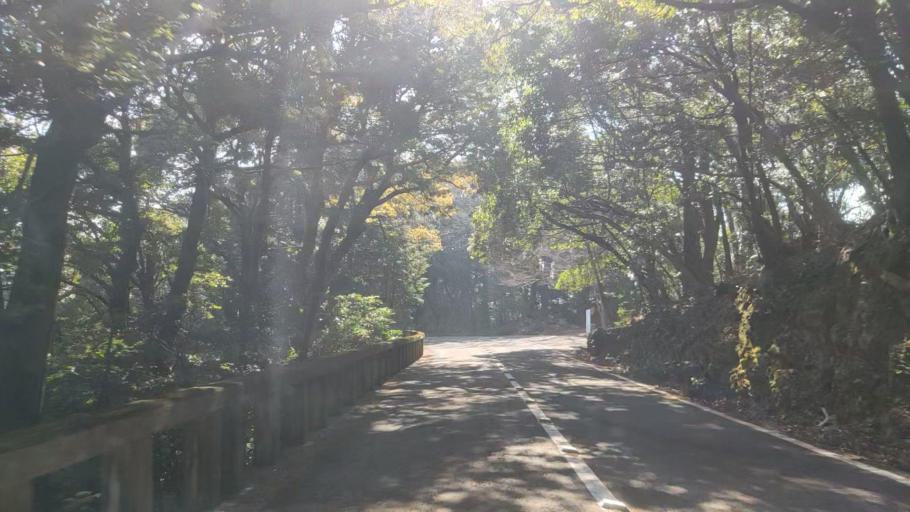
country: JP
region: Gifu
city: Gifu-shi
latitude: 35.4267
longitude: 136.7775
